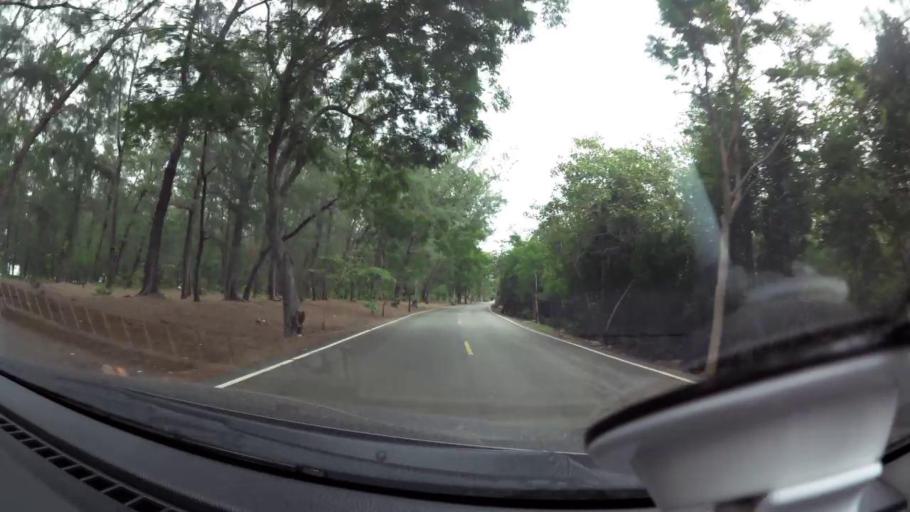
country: TH
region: Prachuap Khiri Khan
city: Pran Buri
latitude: 12.4165
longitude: 99.9846
